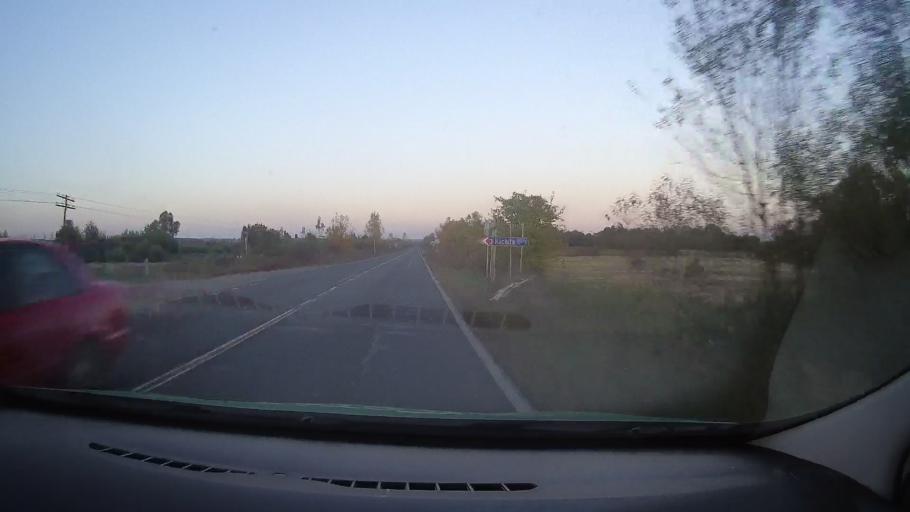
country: RO
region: Timis
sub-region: Comuna Dumbrava
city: Dumbrava
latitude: 45.8406
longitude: 22.1442
